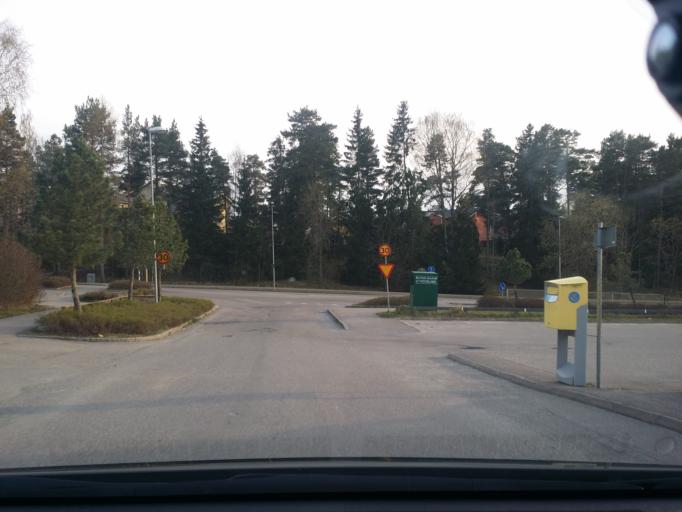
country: SE
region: Uppsala
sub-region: Enkopings Kommun
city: Enkoping
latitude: 59.6307
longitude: 17.1114
